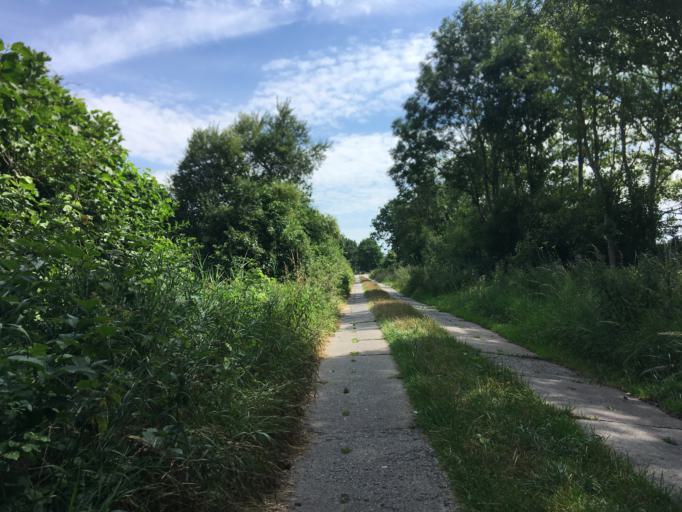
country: DE
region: Brandenburg
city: Zichow
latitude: 53.1949
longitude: 14.0865
